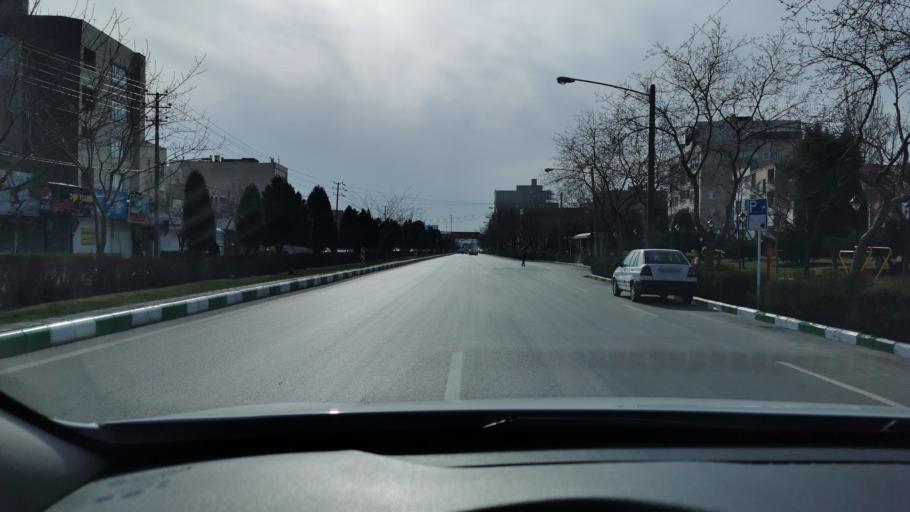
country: IR
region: Razavi Khorasan
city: Mashhad
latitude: 36.2985
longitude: 59.5251
